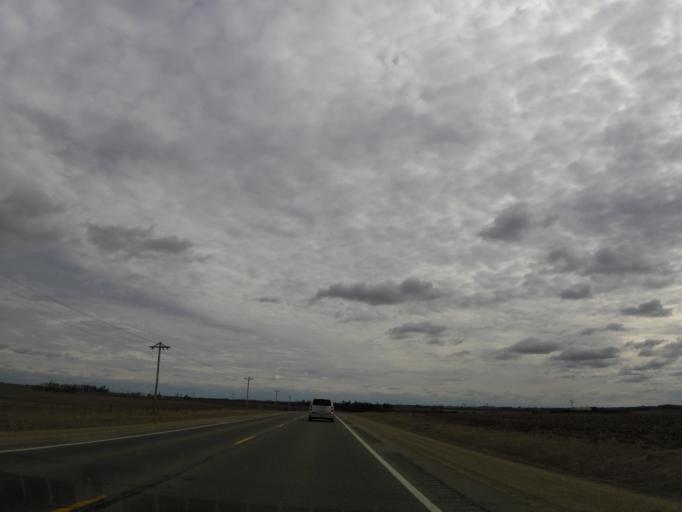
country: US
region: Iowa
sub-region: Chickasaw County
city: New Hampton
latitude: 43.1264
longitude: -92.2980
